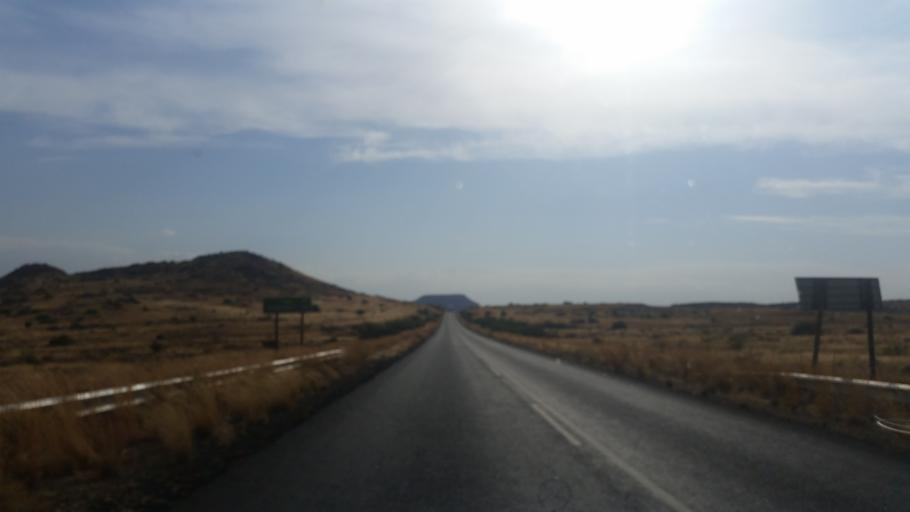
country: ZA
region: Orange Free State
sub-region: Xhariep District Municipality
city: Trompsburg
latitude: -30.4772
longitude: 25.9984
